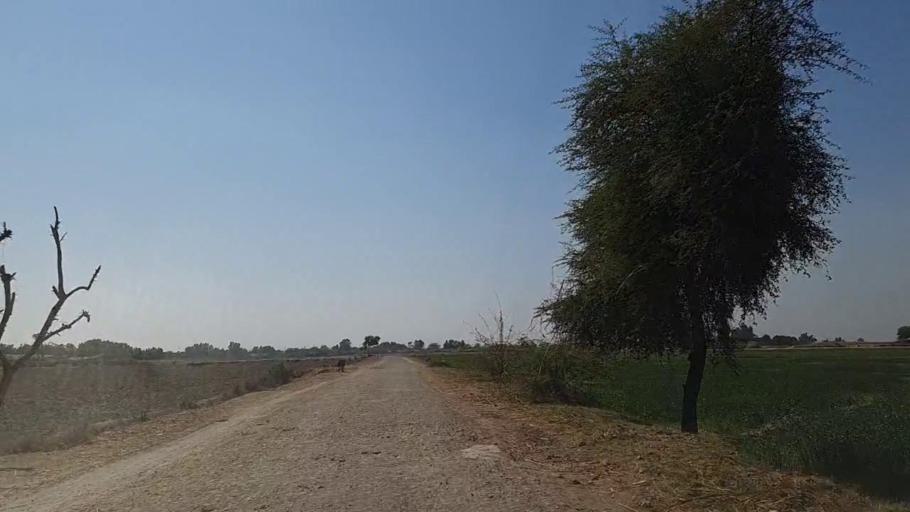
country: PK
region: Sindh
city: Samaro
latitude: 25.3692
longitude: 69.3246
